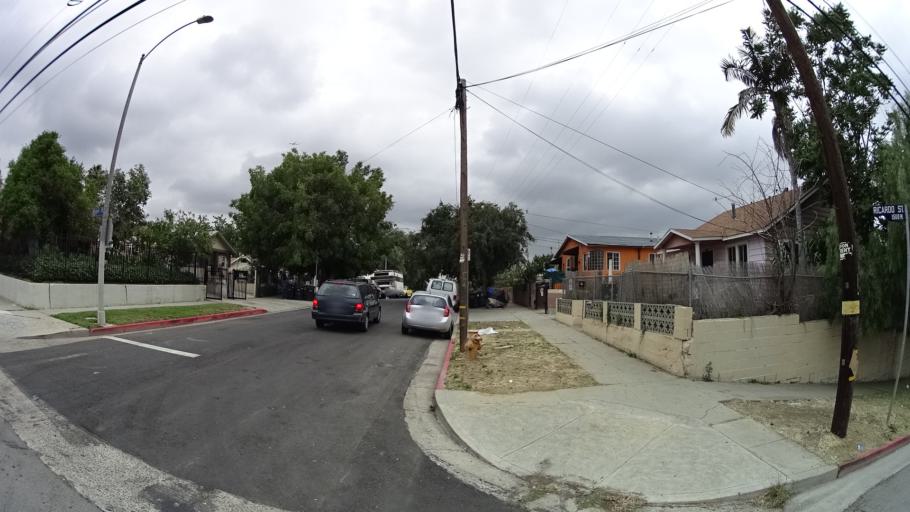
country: US
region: California
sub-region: Los Angeles County
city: Boyle Heights
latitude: 34.0619
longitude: -118.1970
